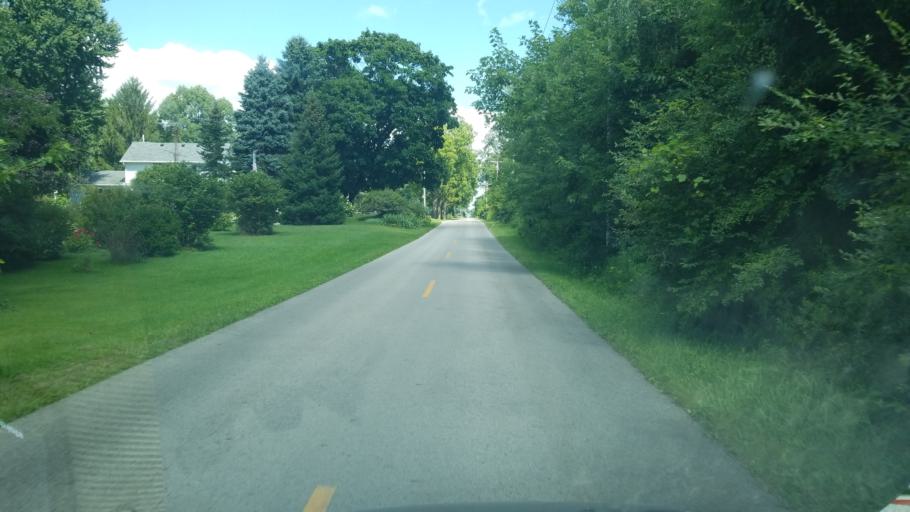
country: US
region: Ohio
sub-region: Henry County
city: Liberty Center
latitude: 41.4768
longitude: -83.9413
